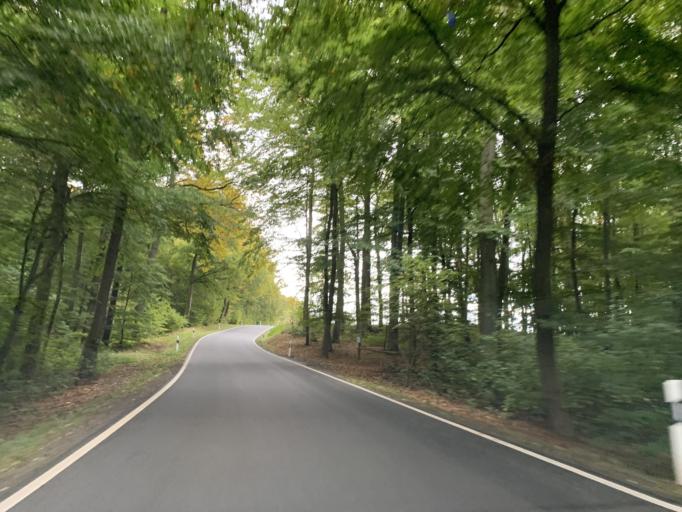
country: DE
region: Mecklenburg-Vorpommern
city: Burg Stargard
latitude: 53.4749
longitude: 13.2907
